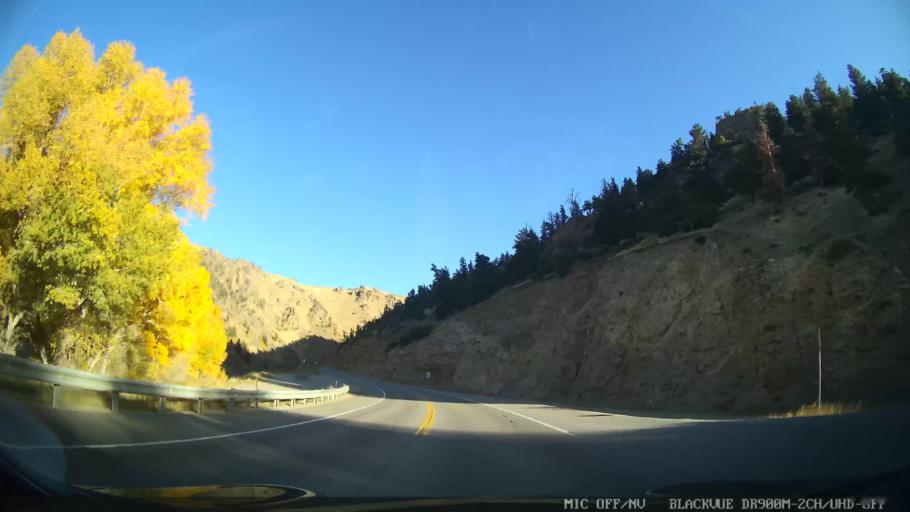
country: US
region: Colorado
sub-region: Grand County
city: Hot Sulphur Springs
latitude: 40.0537
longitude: -106.1327
